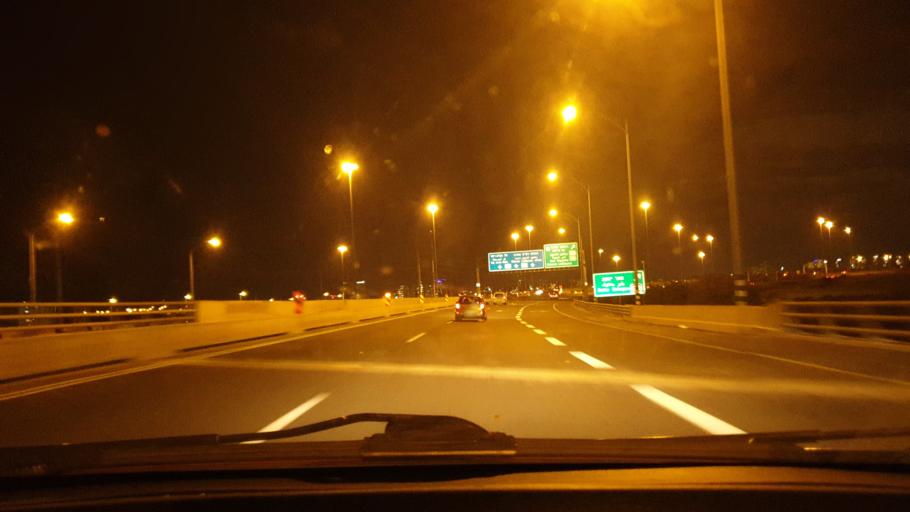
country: IL
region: Central District
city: Ness Ziona
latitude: 31.9339
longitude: 34.8165
